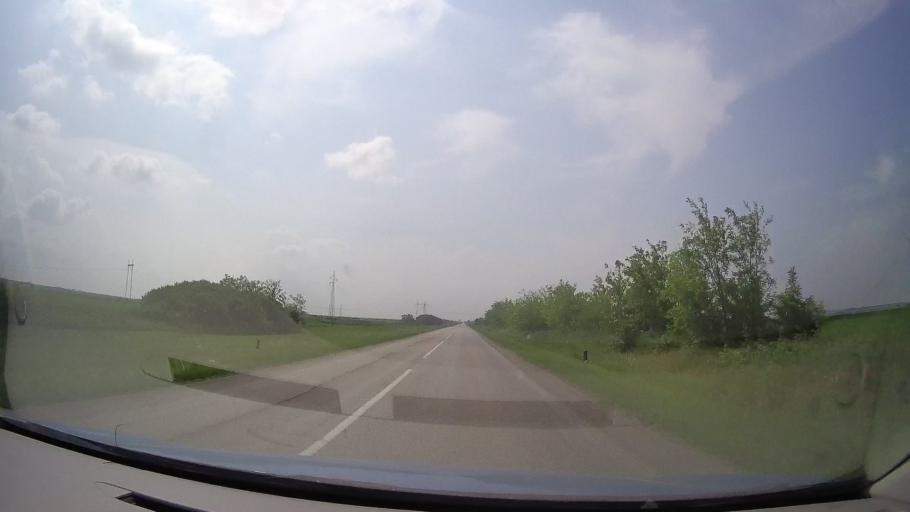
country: RS
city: Crepaja
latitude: 44.9721
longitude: 20.6494
